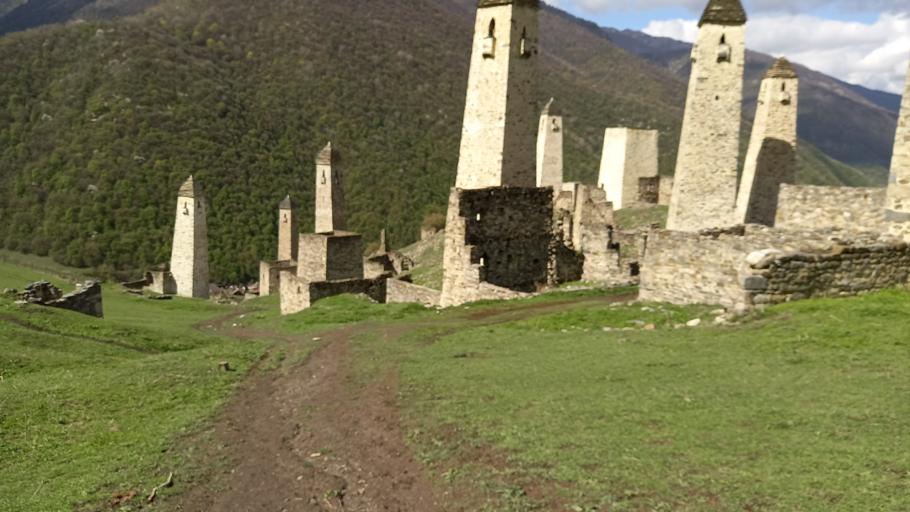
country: RU
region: Ingushetiya
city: Dzhayrakh
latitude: 42.8040
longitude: 44.7608
